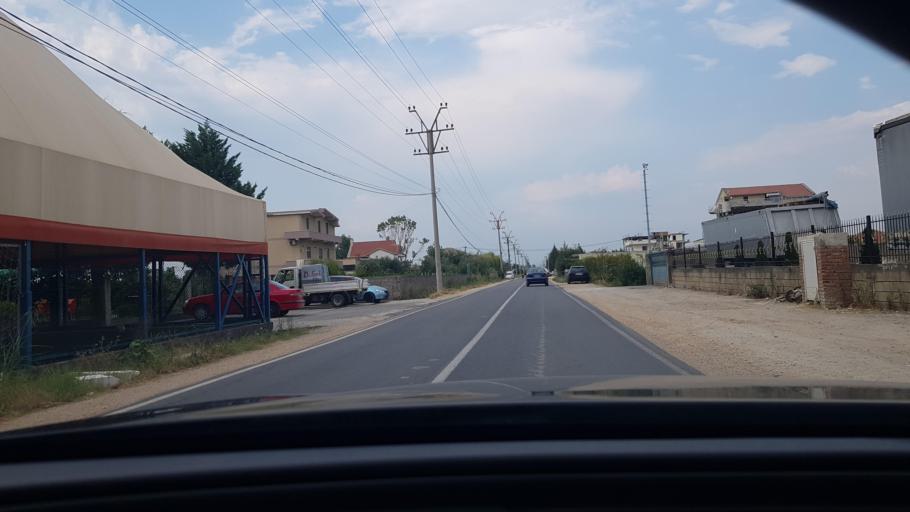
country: AL
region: Durres
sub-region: Rrethi i Durresit
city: Sukth
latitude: 41.4059
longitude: 19.5468
